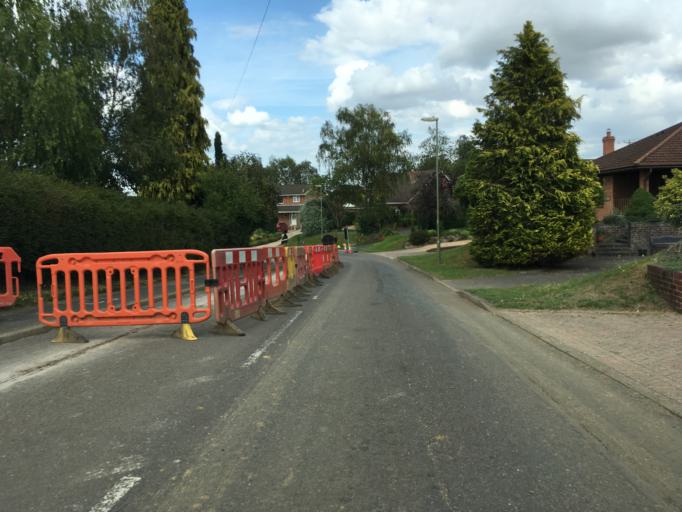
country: GB
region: England
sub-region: Hampshire
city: Overton
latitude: 51.2371
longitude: -1.2636
